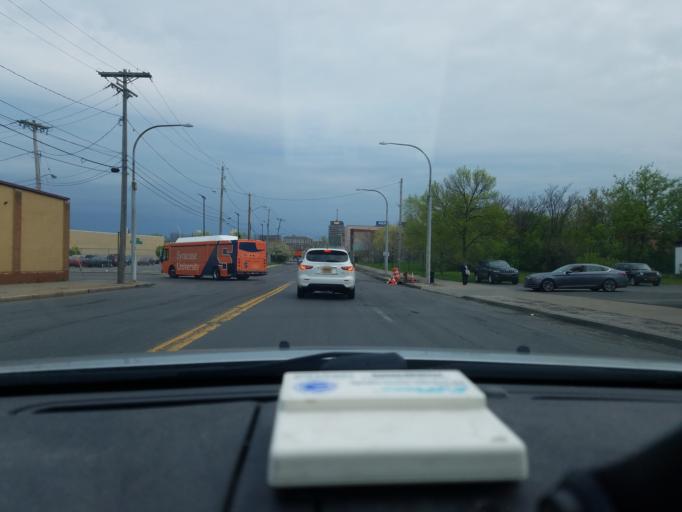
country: US
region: New York
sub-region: Onondaga County
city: Syracuse
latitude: 43.0361
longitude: -76.1495
